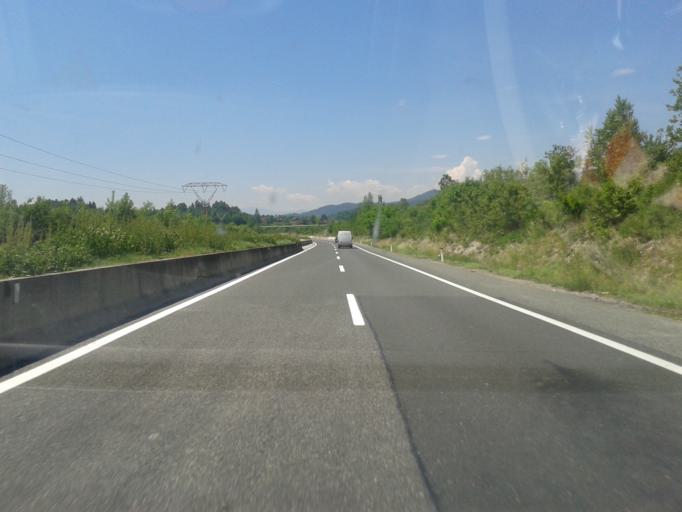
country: AT
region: Carinthia
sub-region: Politischer Bezirk Klagenfurt Land
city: Poggersdorf
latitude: 46.6451
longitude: 14.4178
